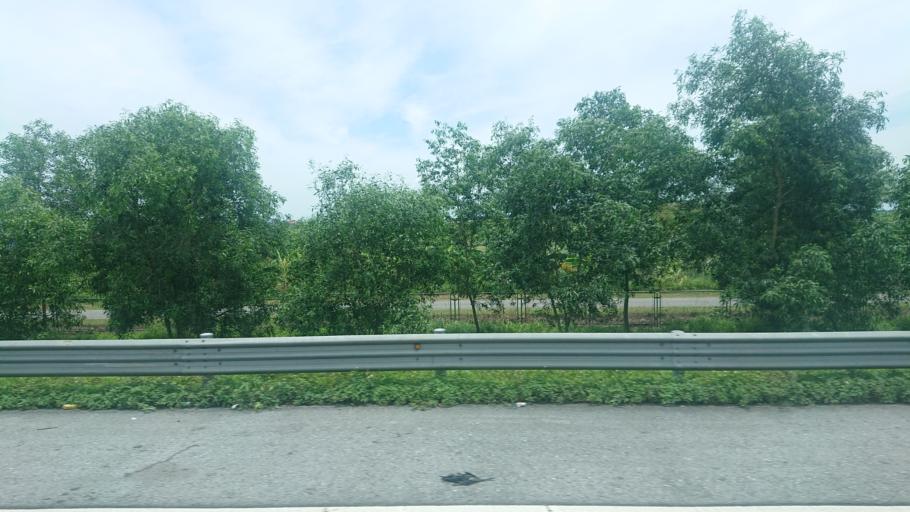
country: VN
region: Hai Phong
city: An Lao
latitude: 20.8184
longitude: 106.4839
